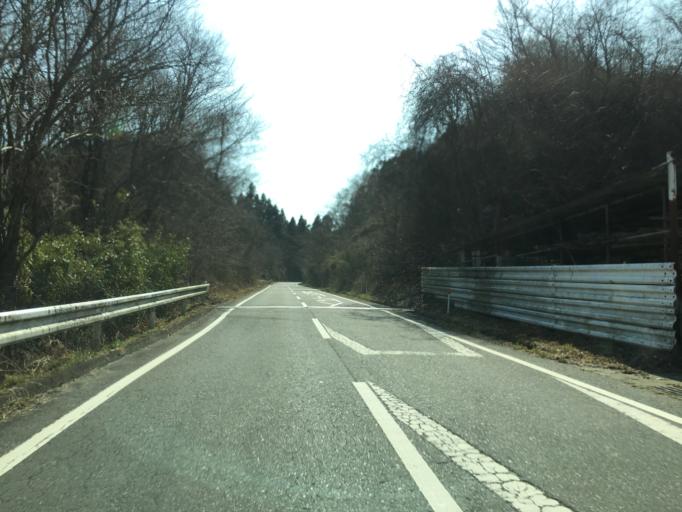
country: JP
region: Ibaraki
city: Daigo
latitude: 36.7931
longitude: 140.4748
